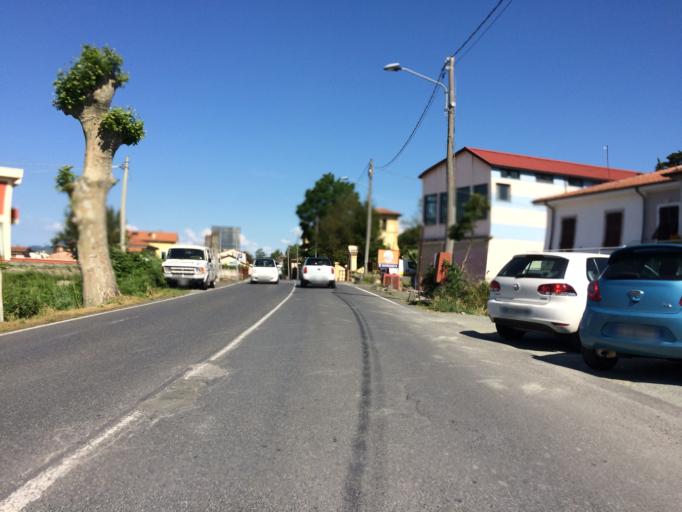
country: IT
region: Liguria
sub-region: Provincia di La Spezia
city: Sarzana
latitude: 44.1043
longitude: 9.9764
